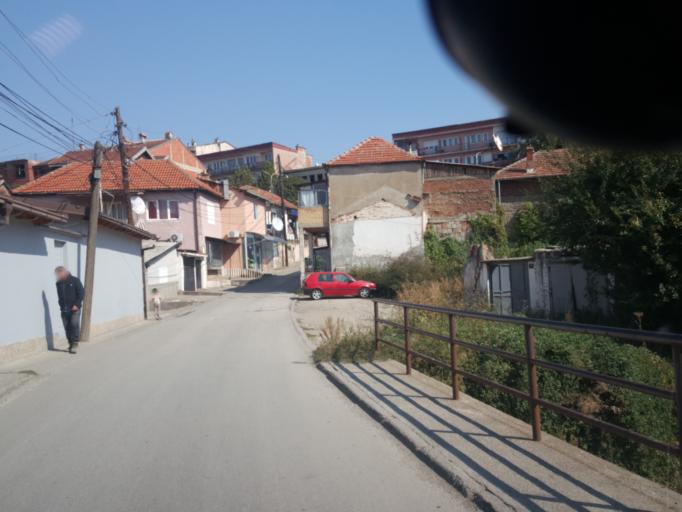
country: XK
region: Gjakova
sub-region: Komuna e Gjakoves
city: Gjakove
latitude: 42.3848
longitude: 20.4269
